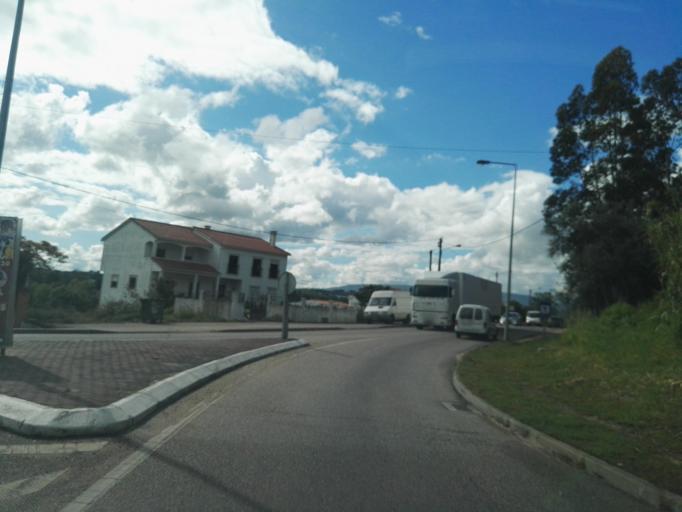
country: PT
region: Santarem
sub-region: Torres Novas
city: Riachos
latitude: 39.4518
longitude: -8.5184
